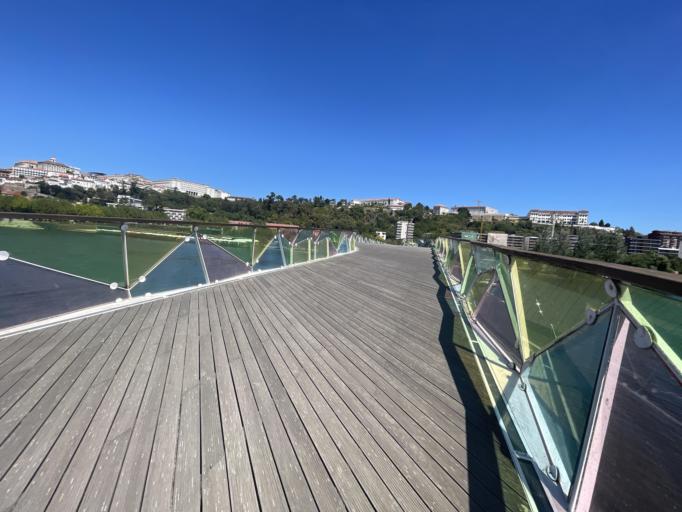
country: PT
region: Coimbra
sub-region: Coimbra
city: Coimbra
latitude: 40.2011
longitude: -8.4273
